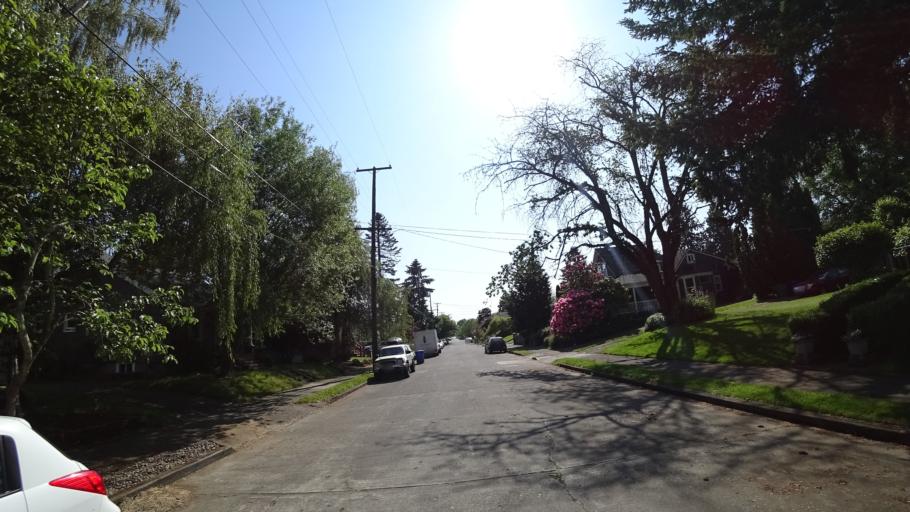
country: US
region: Oregon
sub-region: Multnomah County
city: Portland
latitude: 45.5705
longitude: -122.6455
